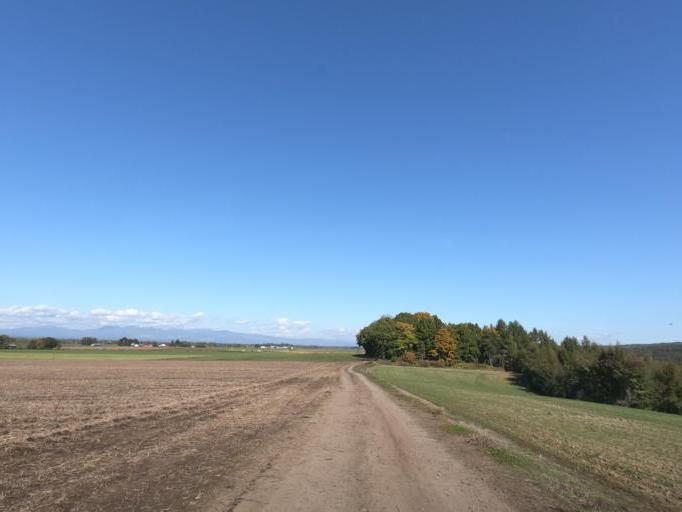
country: JP
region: Hokkaido
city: Otofuke
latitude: 43.0123
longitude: 143.2695
